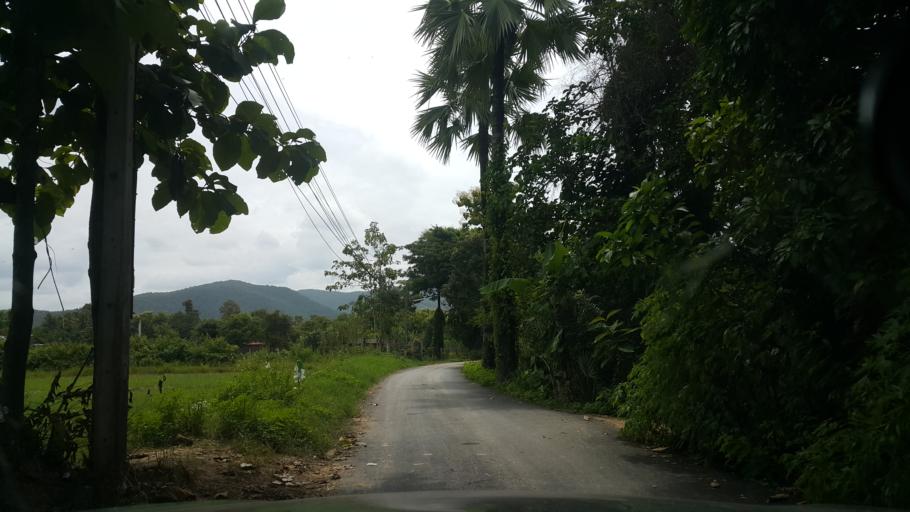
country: TH
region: Chiang Mai
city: San Kamphaeng
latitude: 18.7579
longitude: 99.1722
